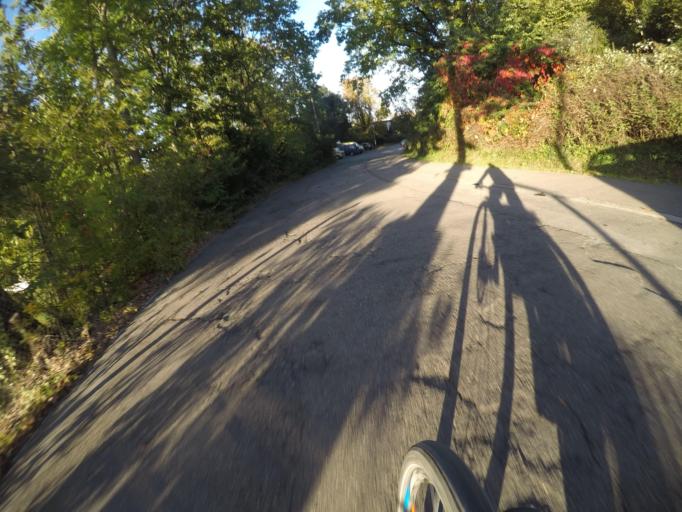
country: DE
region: Baden-Wuerttemberg
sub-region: Regierungsbezirk Stuttgart
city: Stuttgart
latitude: 48.7620
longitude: 9.1823
